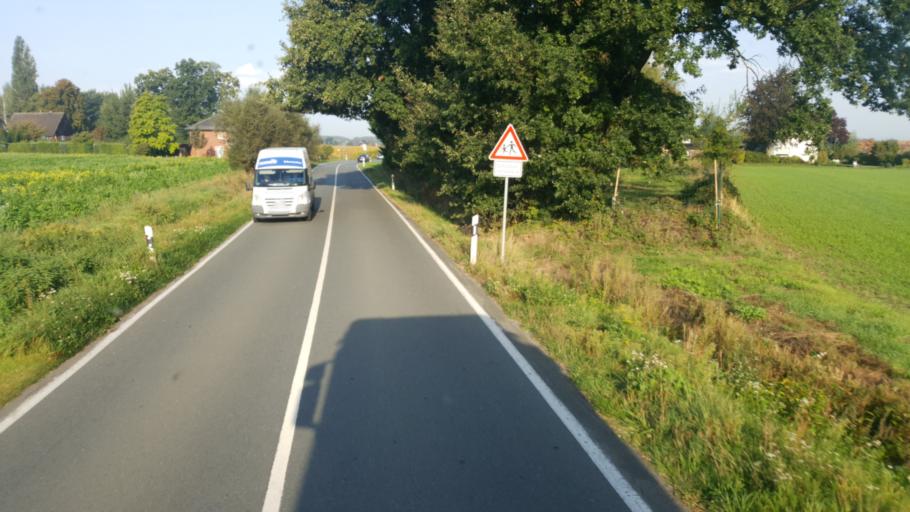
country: DE
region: North Rhine-Westphalia
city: Rietberg
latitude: 51.7396
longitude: 8.3944
